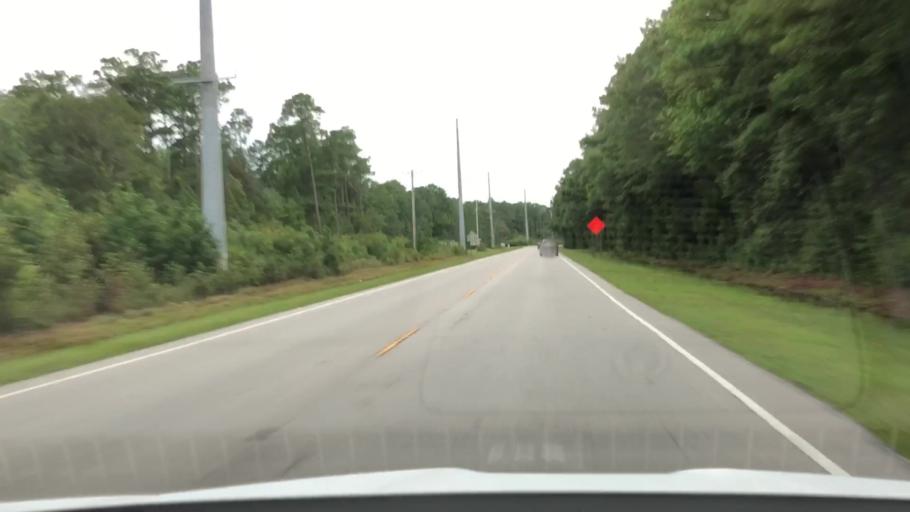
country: US
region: North Carolina
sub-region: Carteret County
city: Cape Carteret
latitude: 34.7456
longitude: -77.0897
